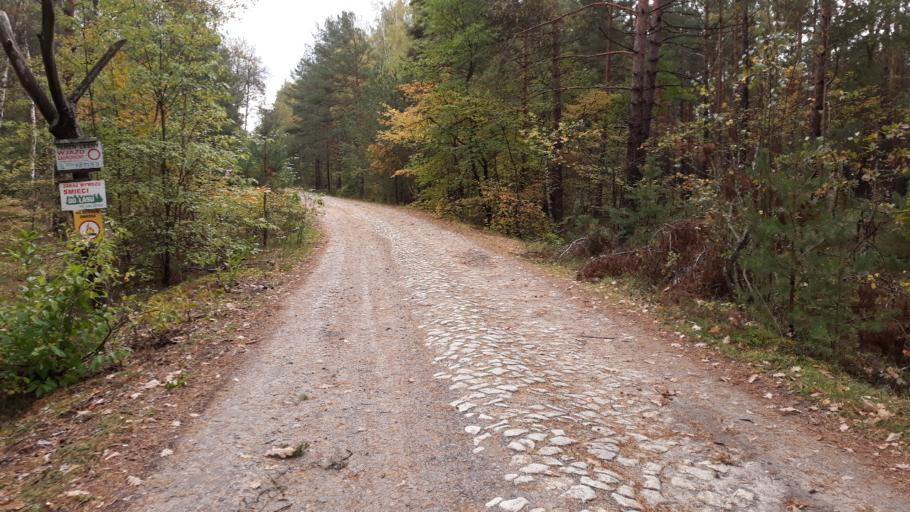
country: PL
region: Lublin Voivodeship
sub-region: Powiat janowski
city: Dzwola
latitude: 50.6466
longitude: 22.5996
